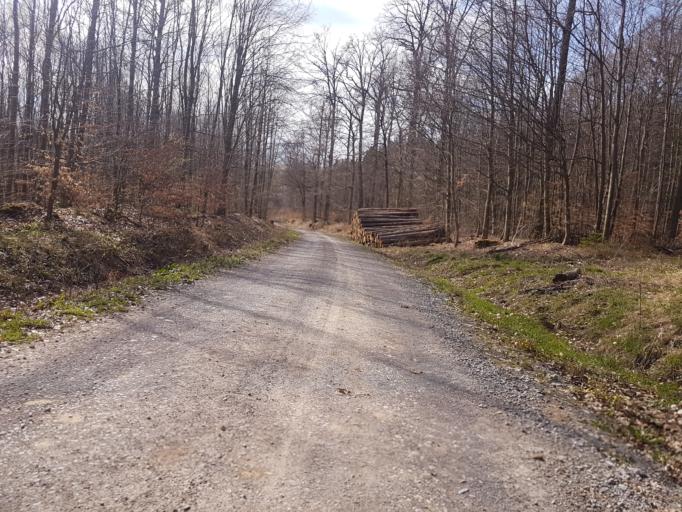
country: DE
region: Baden-Wuerttemberg
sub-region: Regierungsbezirk Stuttgart
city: Forchtenberg
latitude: 49.3253
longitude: 9.5550
